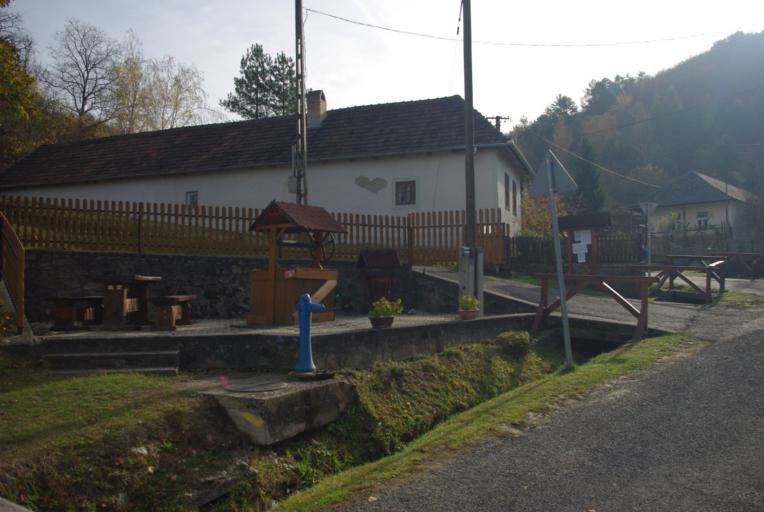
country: HU
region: Borsod-Abauj-Zemplen
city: Sarospatak
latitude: 48.4281
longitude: 21.4934
